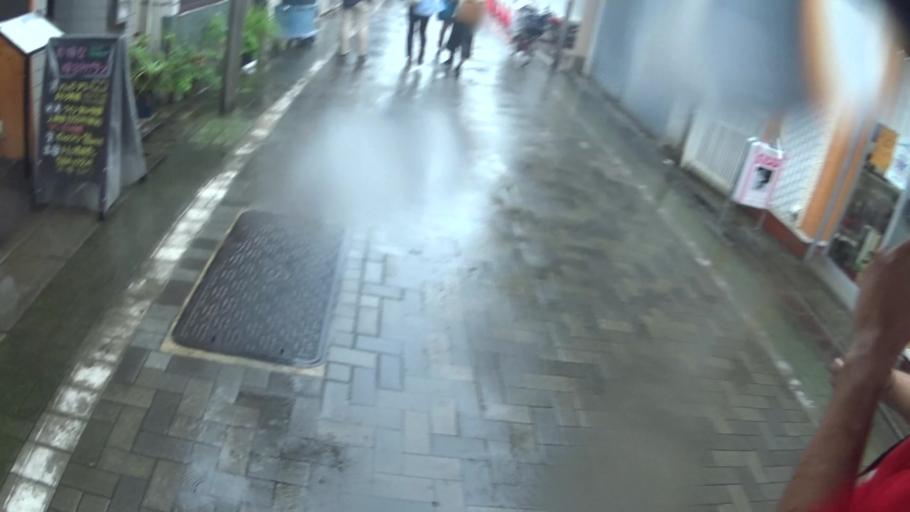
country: JP
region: Tokyo
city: Tokyo
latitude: 35.7405
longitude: 139.6682
